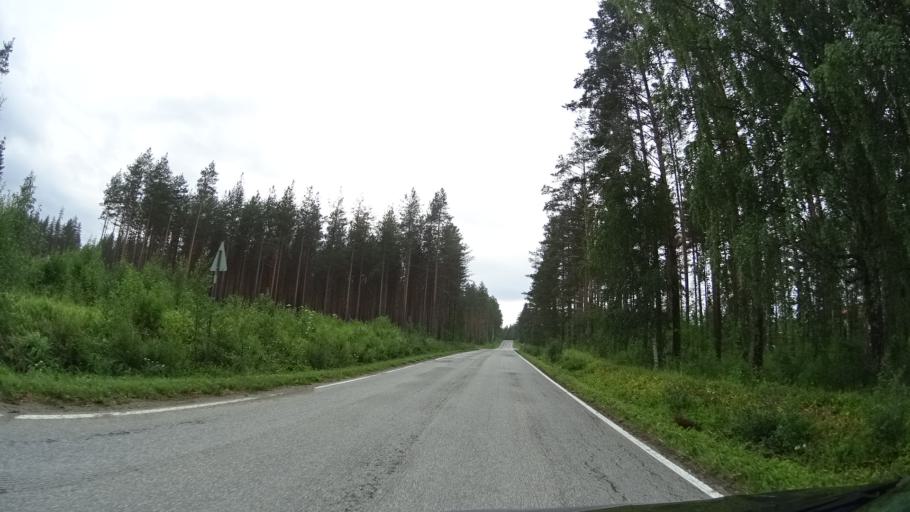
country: FI
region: Southern Savonia
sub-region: Savonlinna
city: Punkaharju
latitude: 61.7474
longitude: 29.4967
